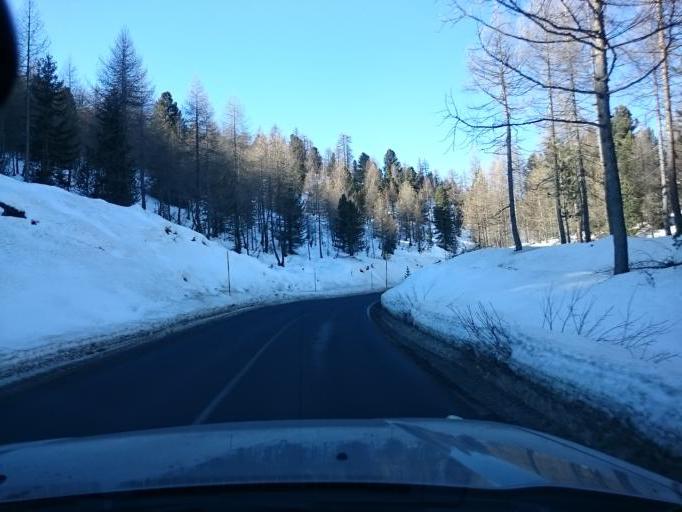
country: IT
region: Lombardy
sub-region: Provincia di Sondrio
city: Isolaccia
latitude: 46.4778
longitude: 10.2488
